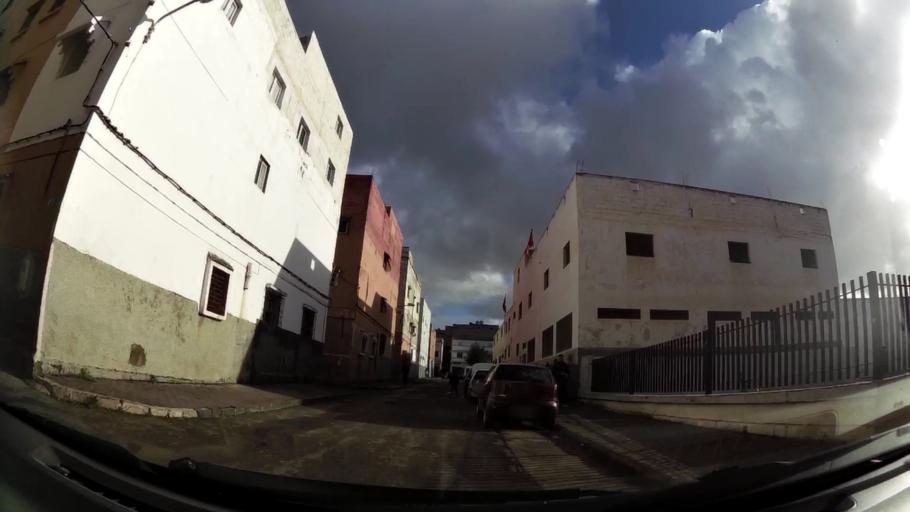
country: MA
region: Grand Casablanca
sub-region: Casablanca
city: Casablanca
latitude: 33.5511
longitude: -7.5965
